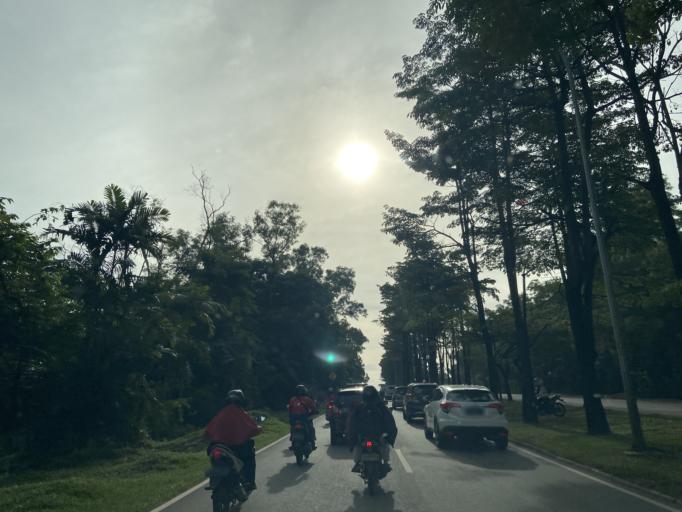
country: SG
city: Singapore
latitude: 1.1319
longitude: 104.0191
